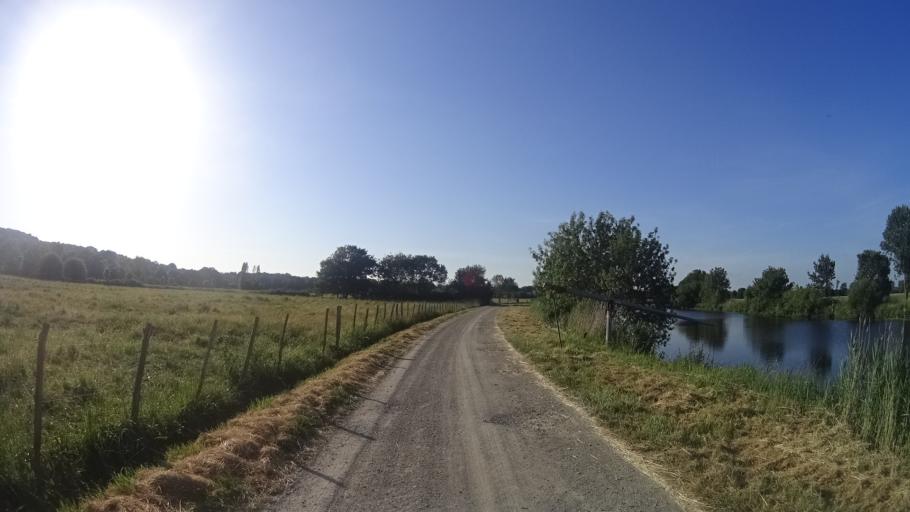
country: FR
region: Brittany
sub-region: Departement du Morbihan
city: Saint-Jean-la-Poterie
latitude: 47.6477
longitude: -2.1140
